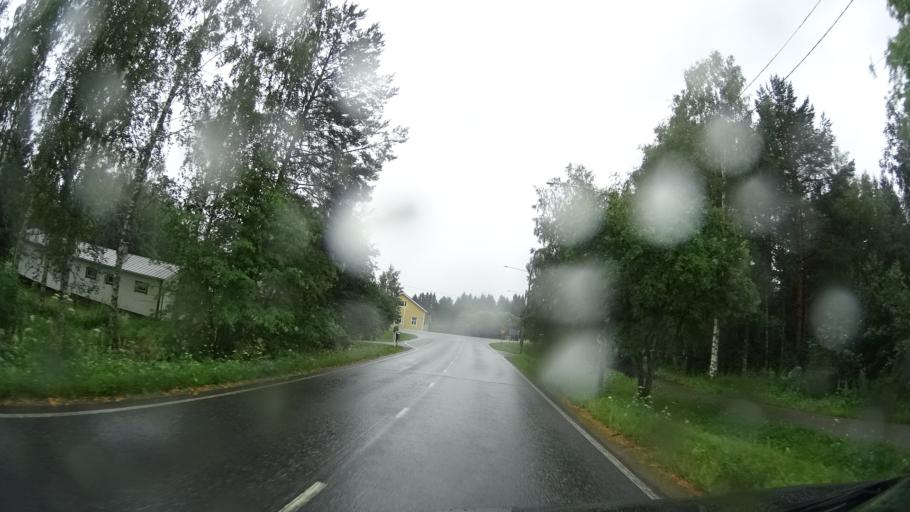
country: FI
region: North Karelia
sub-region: Keski-Karjala
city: Raeaekkylae
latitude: 62.3154
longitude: 29.6067
